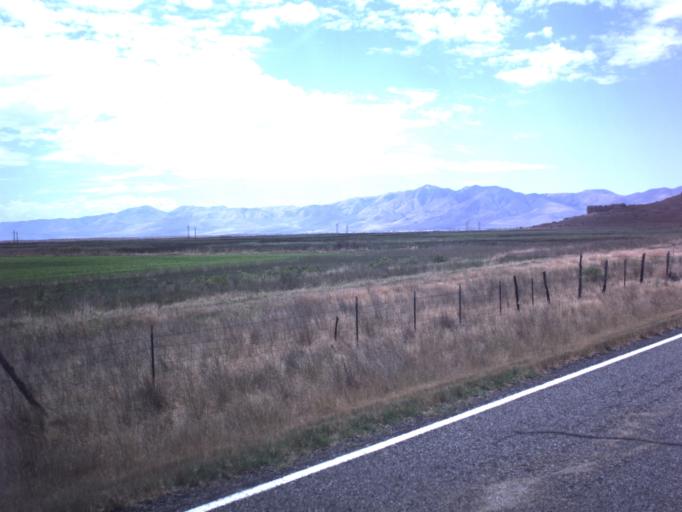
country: US
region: Utah
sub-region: Box Elder County
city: Tremonton
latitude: 41.6211
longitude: -112.3568
